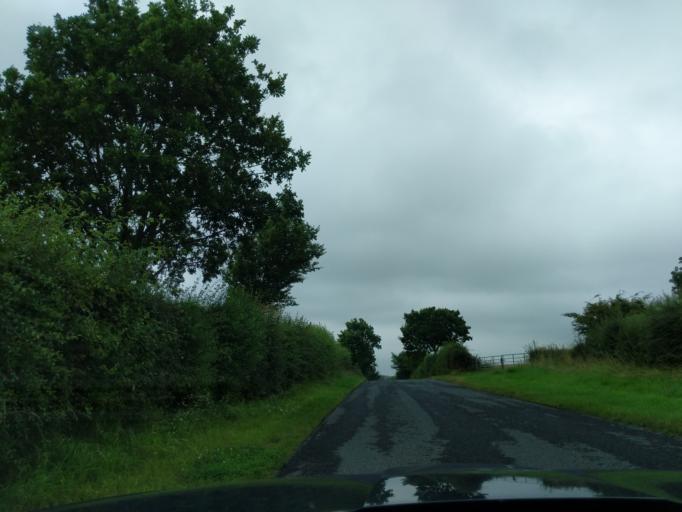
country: GB
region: England
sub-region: Northumberland
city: Ford
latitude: 55.7001
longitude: -2.1434
